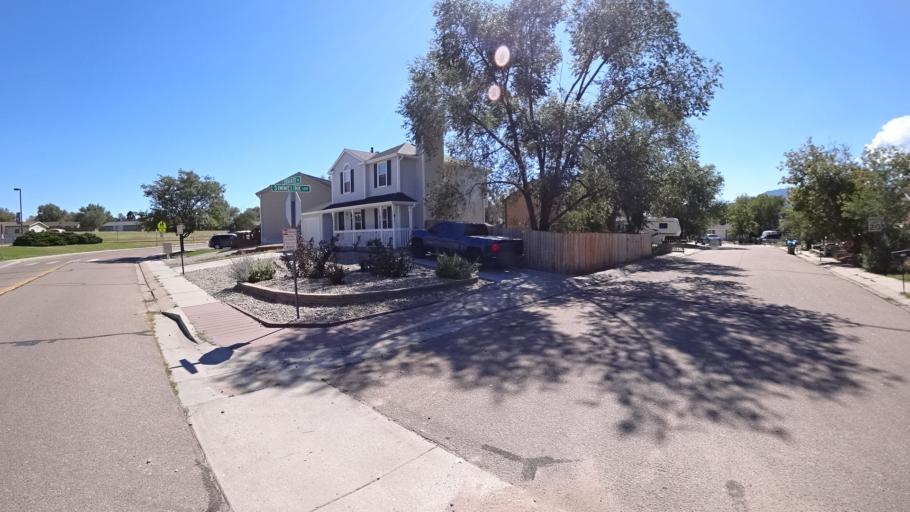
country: US
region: Colorado
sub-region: El Paso County
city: Stratmoor
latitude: 38.7856
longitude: -104.7517
